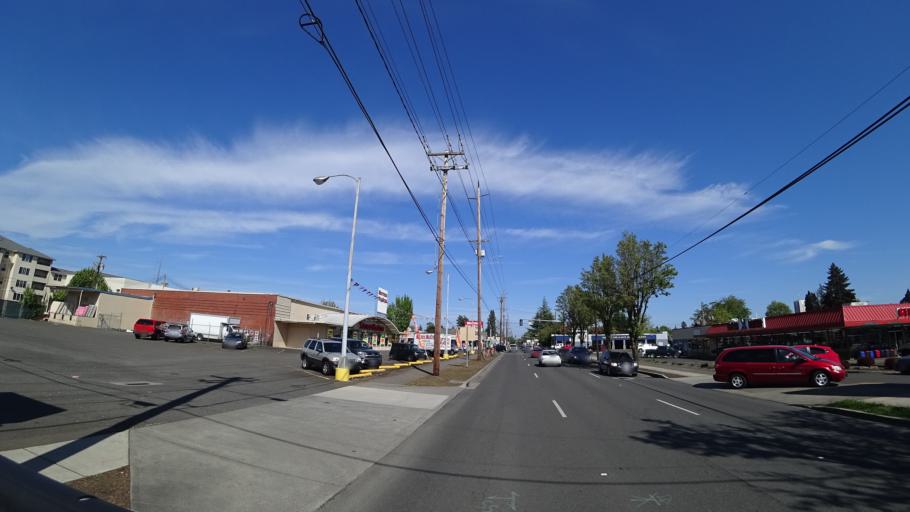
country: US
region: Oregon
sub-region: Washington County
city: Hillsboro
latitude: 45.5201
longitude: -122.9891
